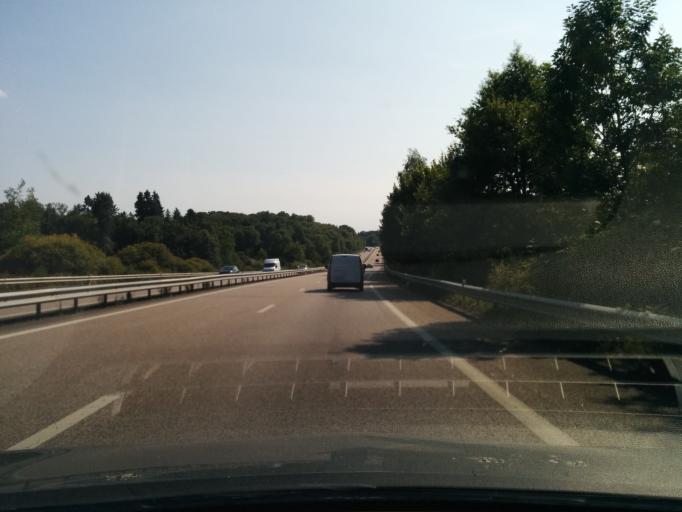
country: FR
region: Limousin
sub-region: Departement de la Haute-Vienne
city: Bonnac-la-Cote
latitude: 45.9473
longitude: 1.3132
